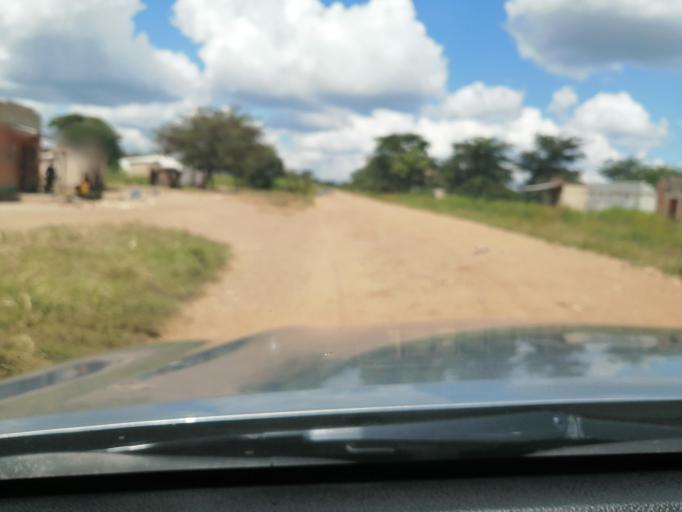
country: ZM
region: Lusaka
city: Lusaka
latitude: -15.1979
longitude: 27.9987
